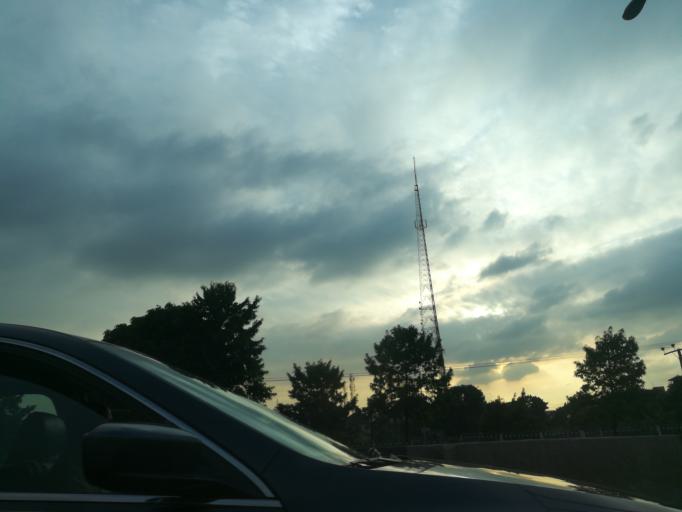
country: NG
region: Lagos
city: Ikeja
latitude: 6.6197
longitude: 3.3647
